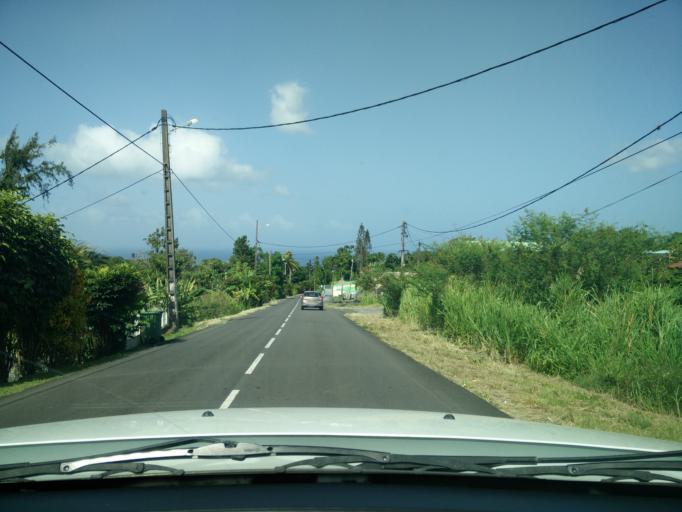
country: GP
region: Guadeloupe
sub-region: Guadeloupe
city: Gourbeyre
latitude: 15.9970
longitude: -61.7021
